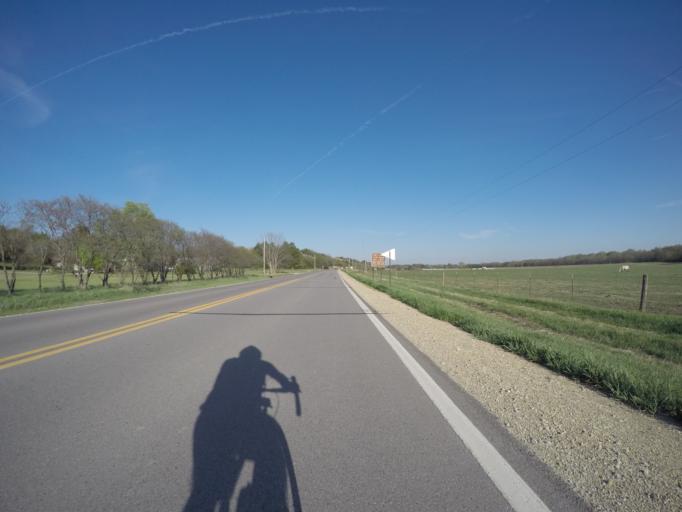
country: US
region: Kansas
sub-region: Riley County
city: Ogden
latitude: 39.2292
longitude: -96.7229
